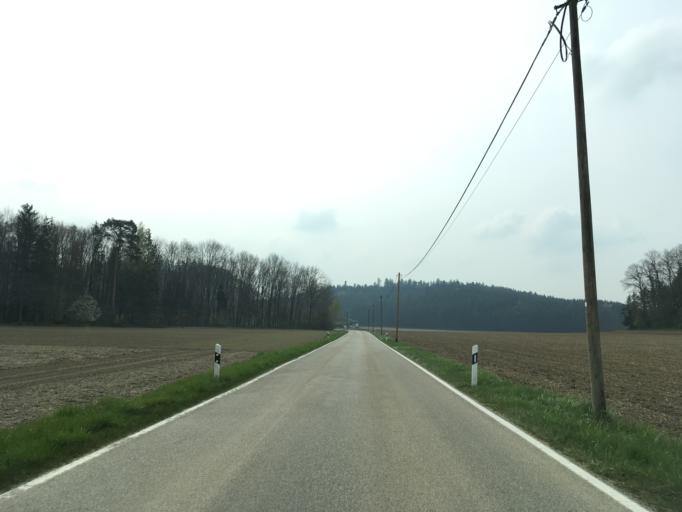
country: DE
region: Bavaria
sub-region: Upper Bavaria
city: Jettenbach
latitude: 48.1608
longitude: 12.3795
